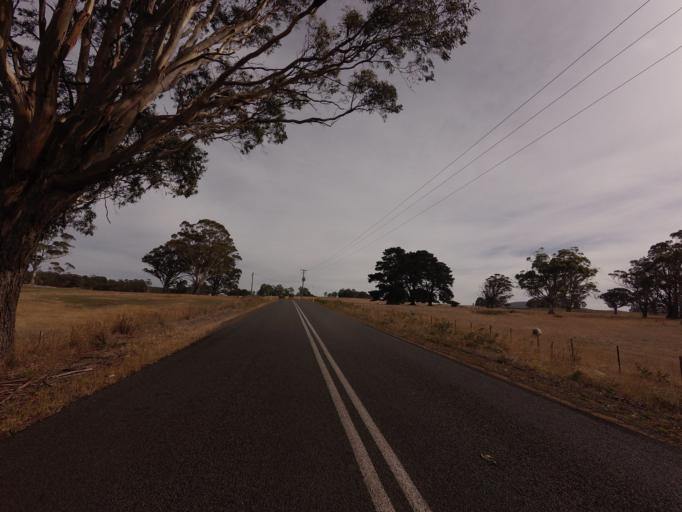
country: AU
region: Tasmania
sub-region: Sorell
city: Sorell
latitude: -42.4083
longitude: 147.4545
